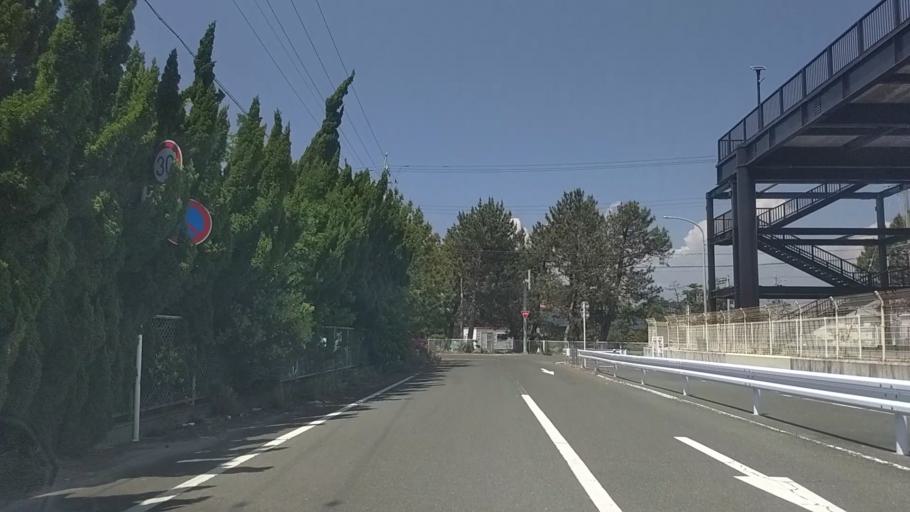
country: JP
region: Shizuoka
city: Kosai-shi
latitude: 34.6820
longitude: 137.5851
